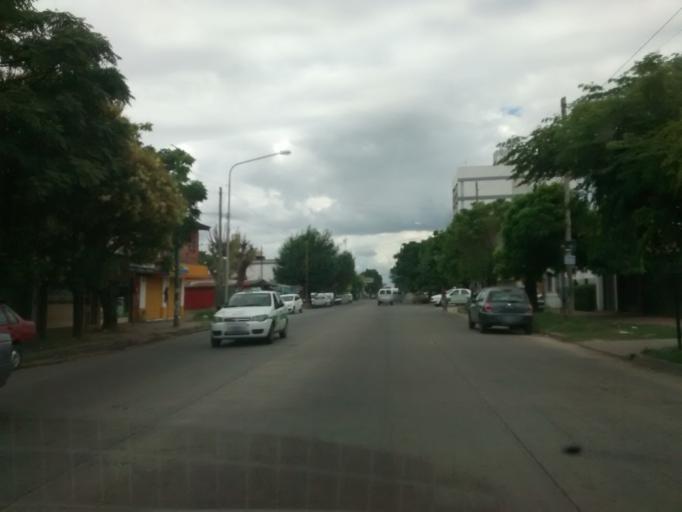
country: AR
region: Buenos Aires
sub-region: Partido de La Plata
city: La Plata
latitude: -34.9163
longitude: -57.9147
